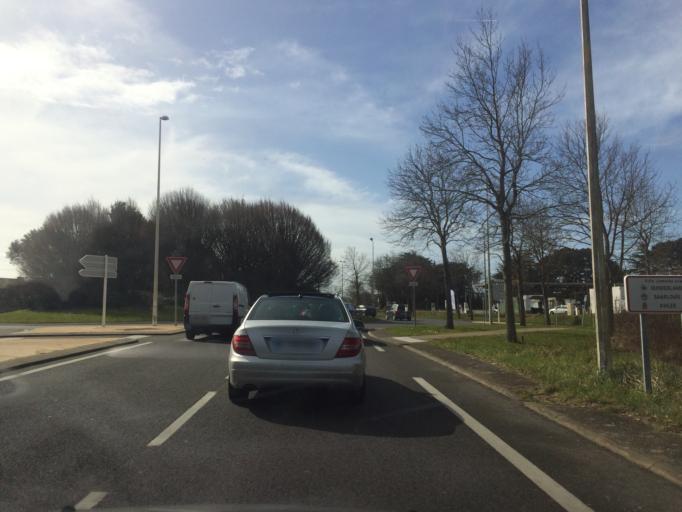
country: FR
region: Pays de la Loire
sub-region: Departement de la Loire-Atlantique
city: Saint-Nazaire
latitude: 47.2720
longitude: -2.2494
